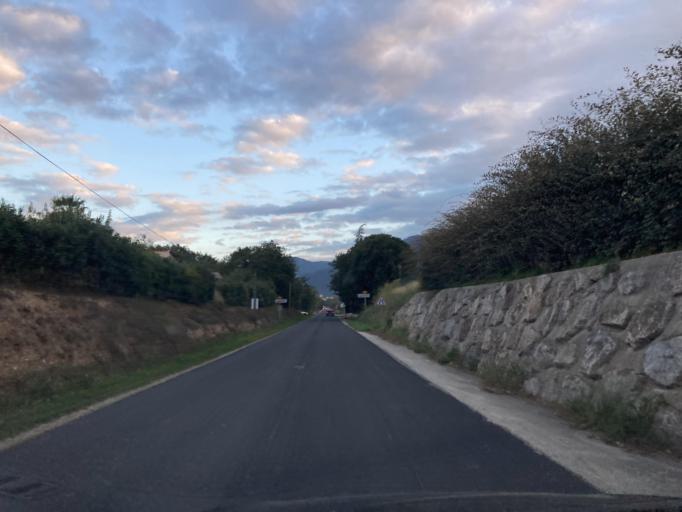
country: FR
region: Languedoc-Roussillon
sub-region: Departement des Pyrenees-Orientales
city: Sant Genis de Fontanes
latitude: 42.5639
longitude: 2.9012
